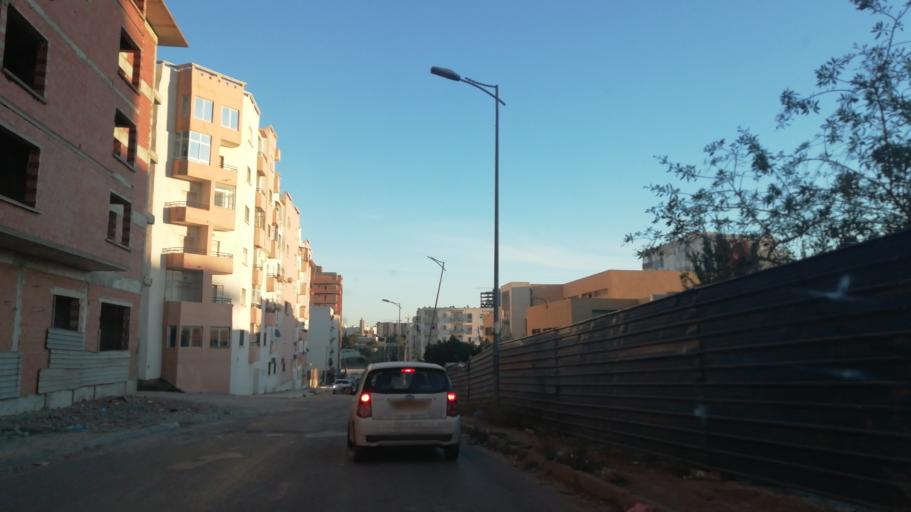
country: DZ
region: Oran
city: Bir el Djir
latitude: 35.7181
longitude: -0.5760
